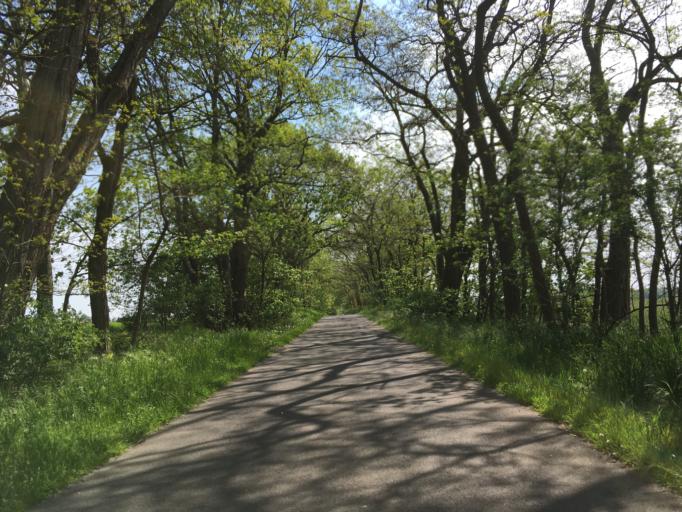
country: DE
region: Brandenburg
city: Werneuchen
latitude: 52.6013
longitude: 13.7314
